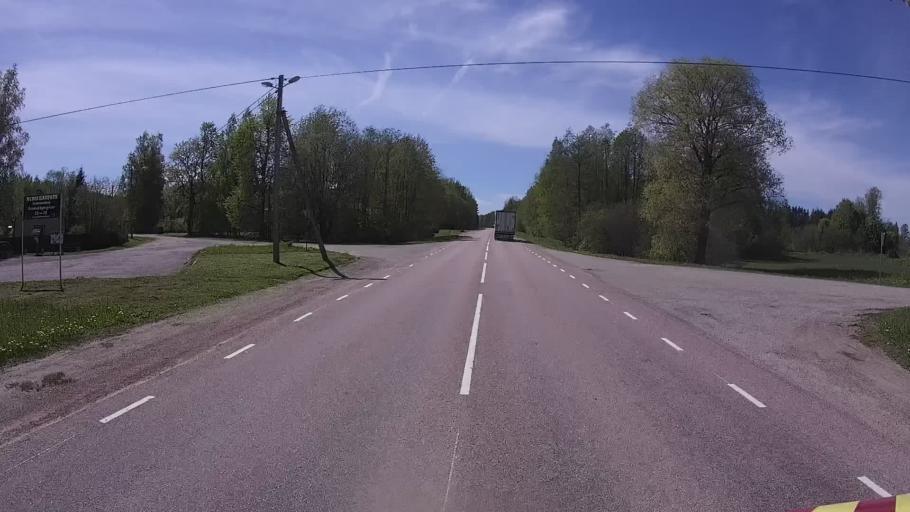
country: EE
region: Vorumaa
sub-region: Voru linn
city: Voru
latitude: 57.7782
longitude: 26.8757
